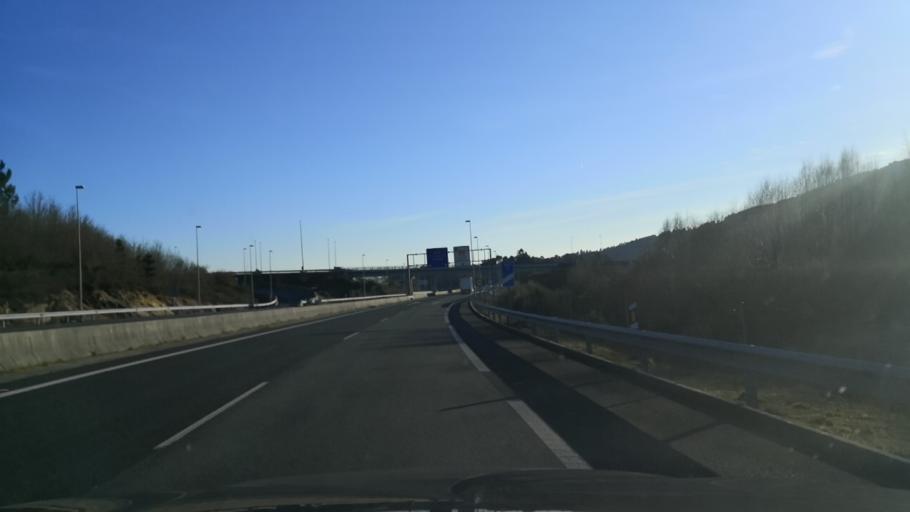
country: ES
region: Galicia
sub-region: Provincia de Ourense
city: Pinor
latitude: 42.5258
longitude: -8.0168
